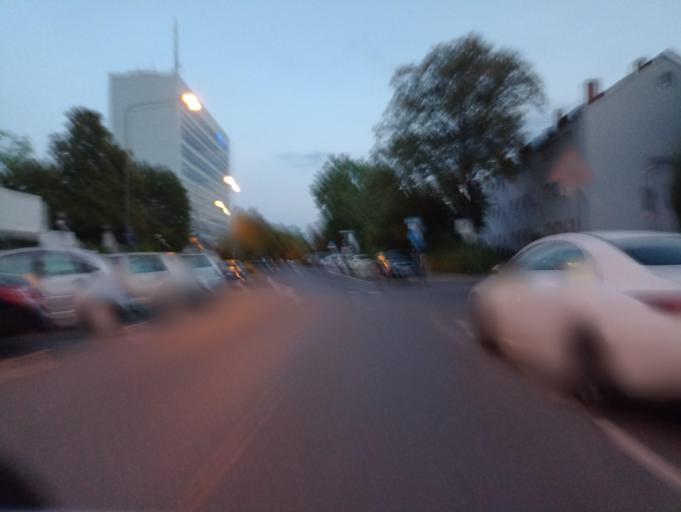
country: DE
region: Hesse
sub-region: Regierungsbezirk Darmstadt
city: Frankfurt am Main
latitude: 50.1357
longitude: 8.6751
